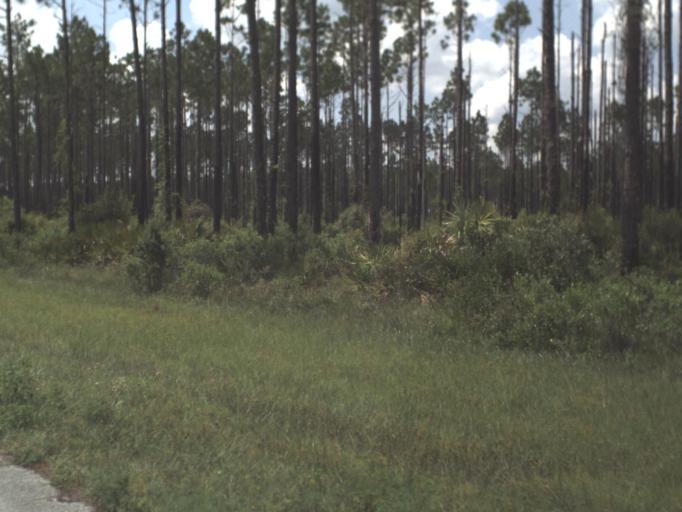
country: US
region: Florida
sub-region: Baker County
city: Macclenny
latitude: 30.5507
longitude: -82.3603
